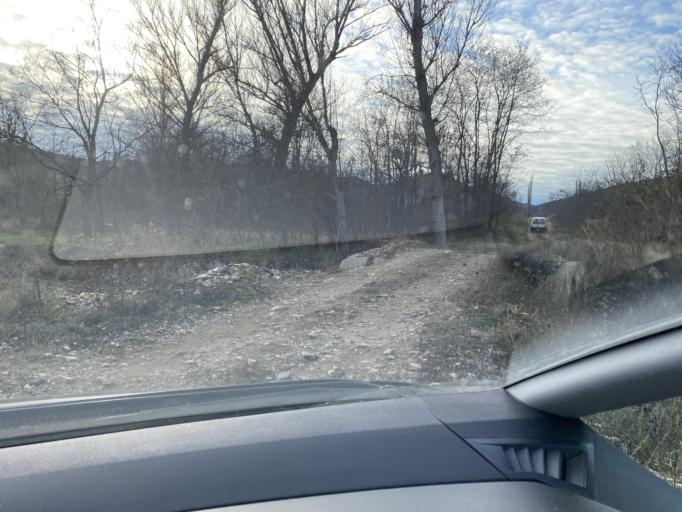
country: MK
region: Opstina Rankovce
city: Rankovce
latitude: 42.1537
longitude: 22.0852
